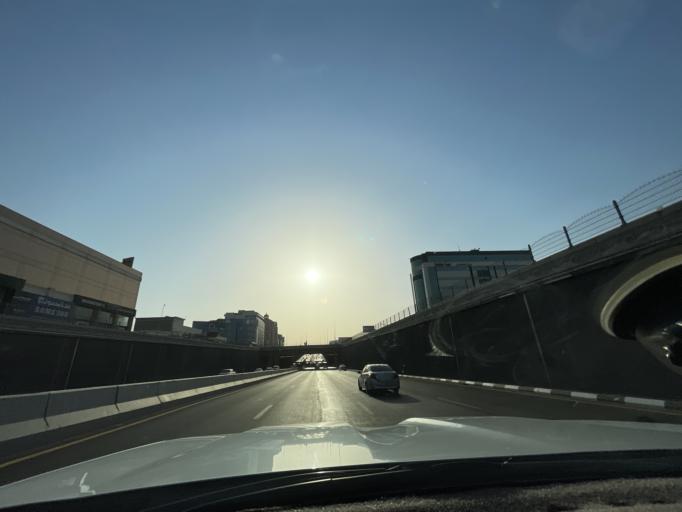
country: SA
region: Eastern Province
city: Khobar
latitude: 26.2857
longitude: 50.1917
